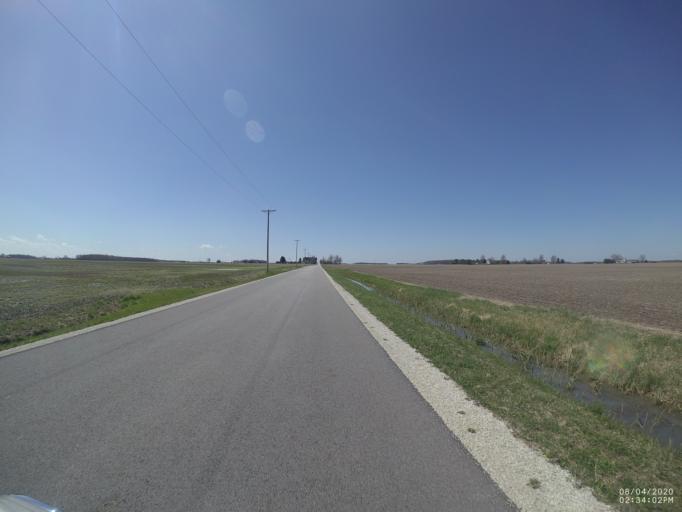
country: US
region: Ohio
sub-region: Sandusky County
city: Gibsonburg
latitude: 41.2823
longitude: -83.2773
